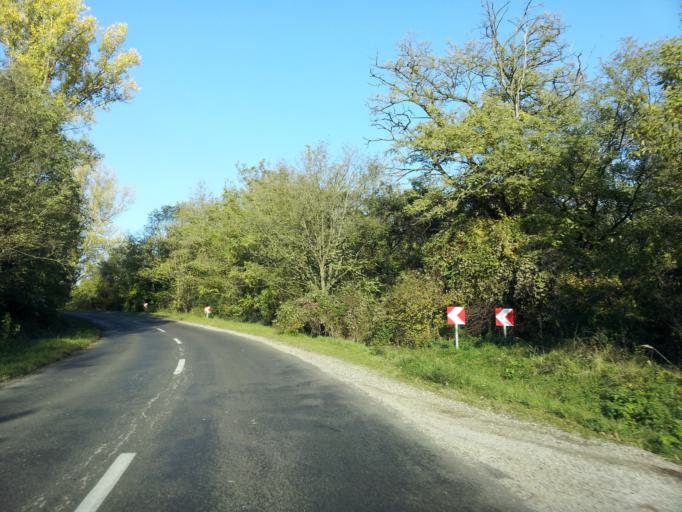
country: HU
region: Fejer
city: Bodajk
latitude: 47.3191
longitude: 18.2096
